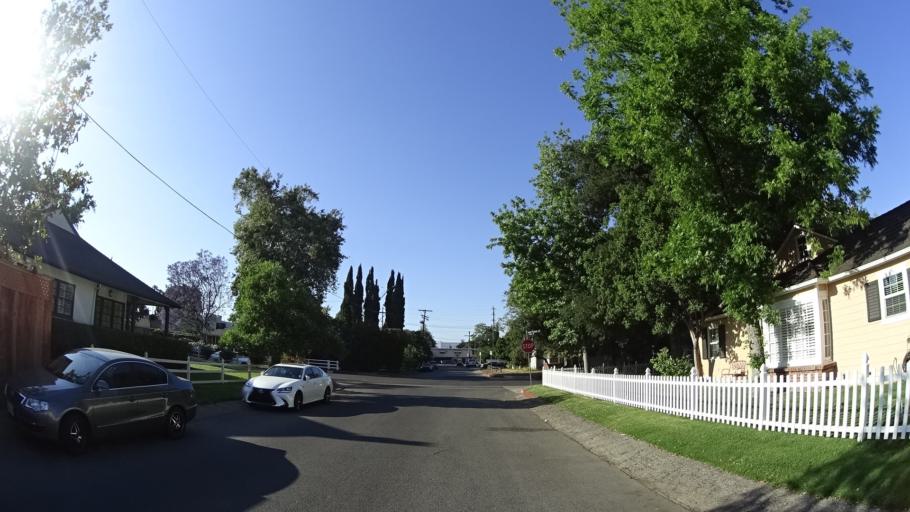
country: US
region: California
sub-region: Los Angeles County
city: North Hollywood
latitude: 34.1636
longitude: -118.3985
